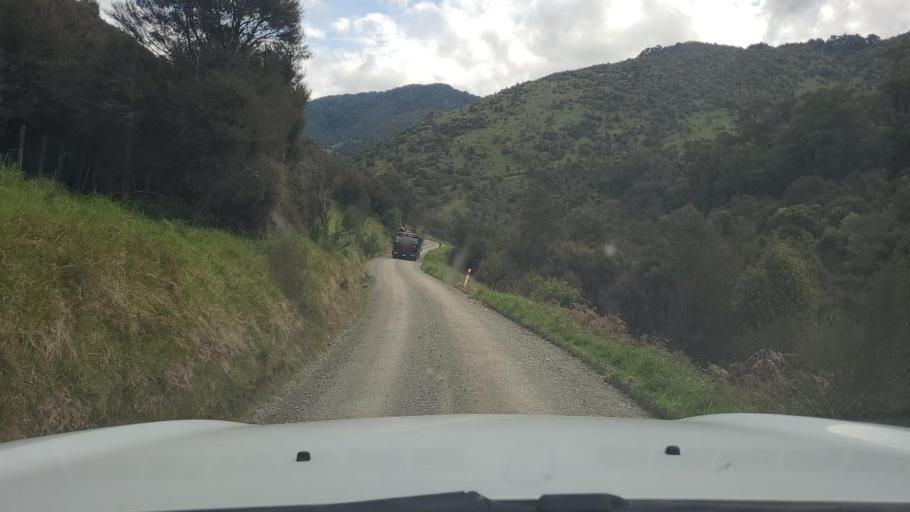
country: NZ
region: Wellington
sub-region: Masterton District
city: Masterton
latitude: -40.9337
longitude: 175.4840
